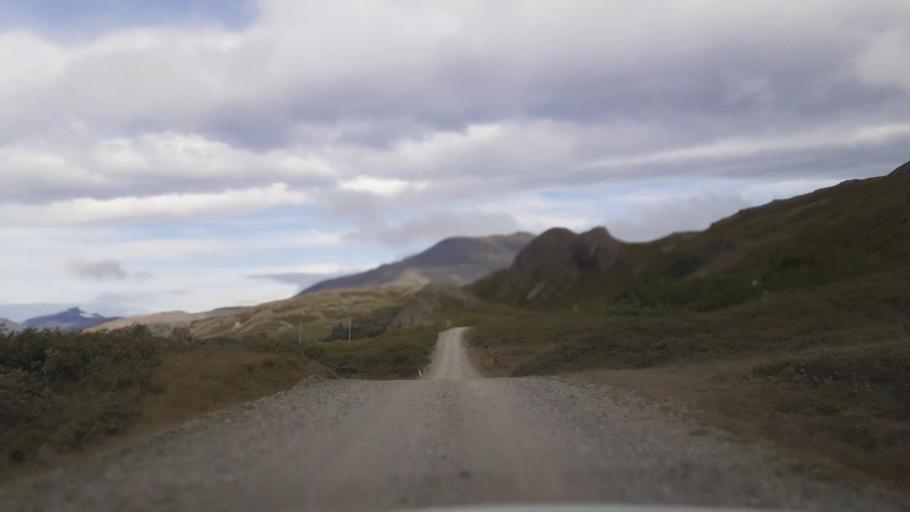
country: IS
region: East
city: Hoefn
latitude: 64.4270
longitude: -14.8838
